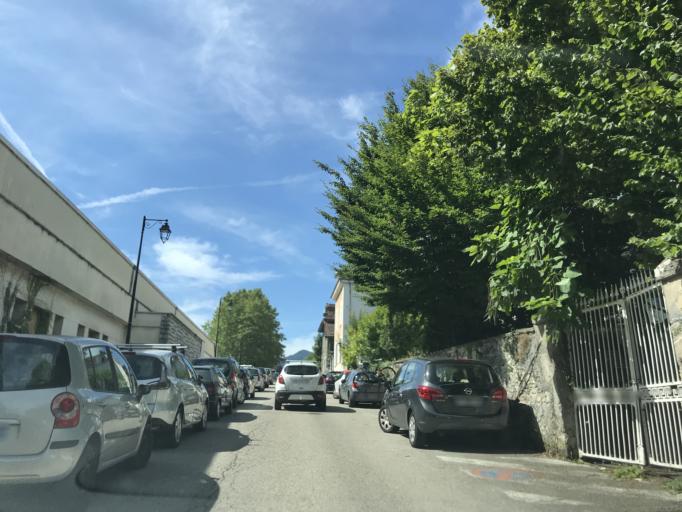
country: FR
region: Rhone-Alpes
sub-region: Departement de l'Isere
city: Allevard
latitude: 45.3920
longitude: 6.0723
